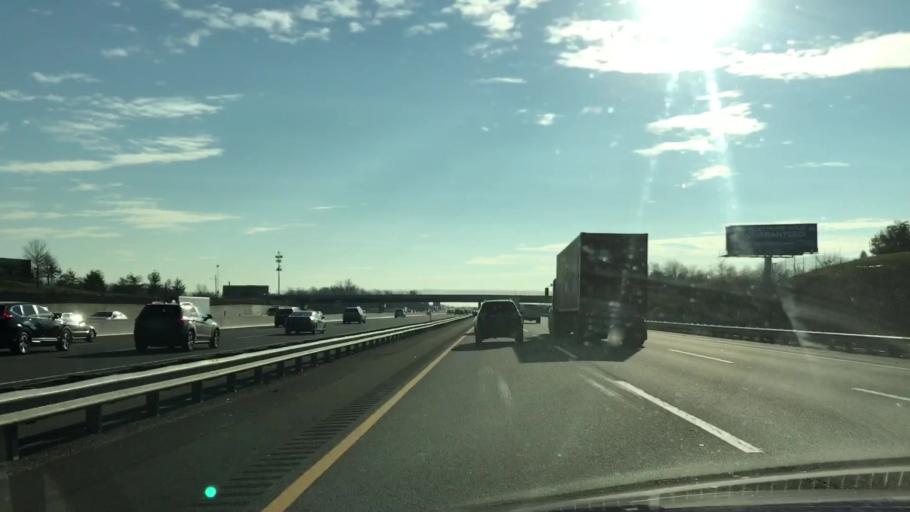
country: US
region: New Jersey
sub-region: Middlesex County
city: Cranbury
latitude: 40.3073
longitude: -74.4930
